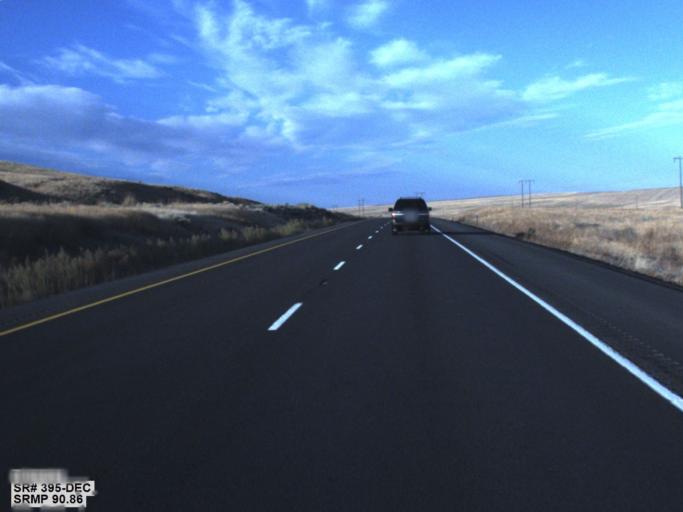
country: US
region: Washington
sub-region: Adams County
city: Ritzville
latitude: 47.0503
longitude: -118.4328
